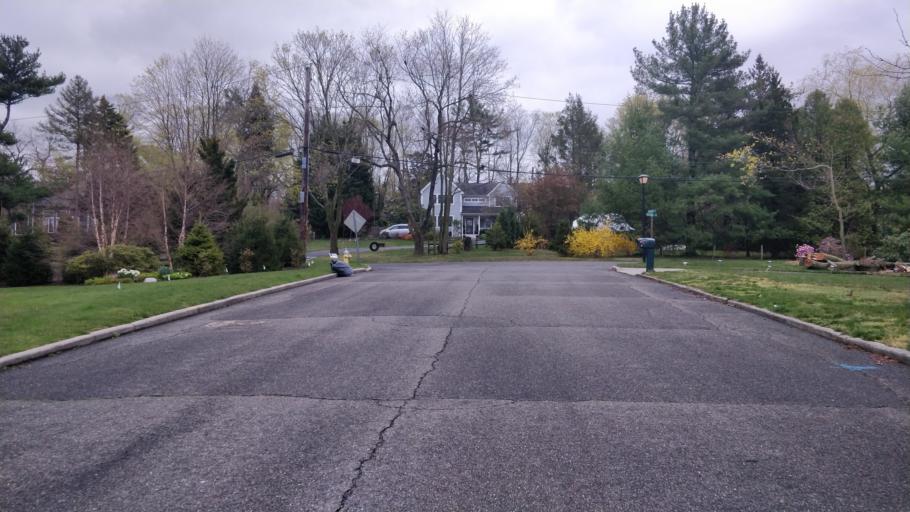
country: US
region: New York
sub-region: Suffolk County
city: East Setauket
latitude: 40.9482
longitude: -73.0968
